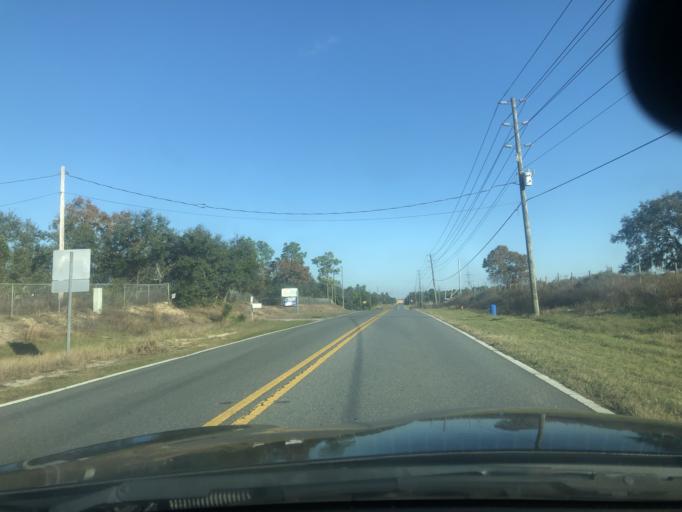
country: US
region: Florida
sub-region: Citrus County
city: Sugarmill Woods
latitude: 28.7640
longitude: -82.5217
